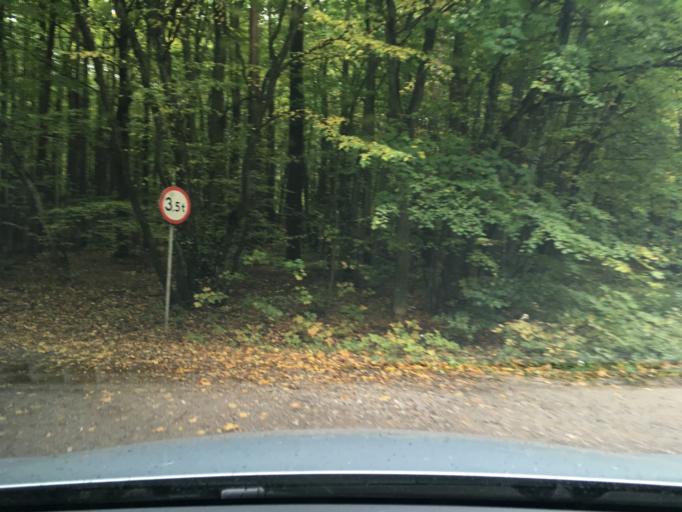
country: PL
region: Pomeranian Voivodeship
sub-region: Powiat koscierski
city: Koscierzyna
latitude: 54.0983
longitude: 17.9770
